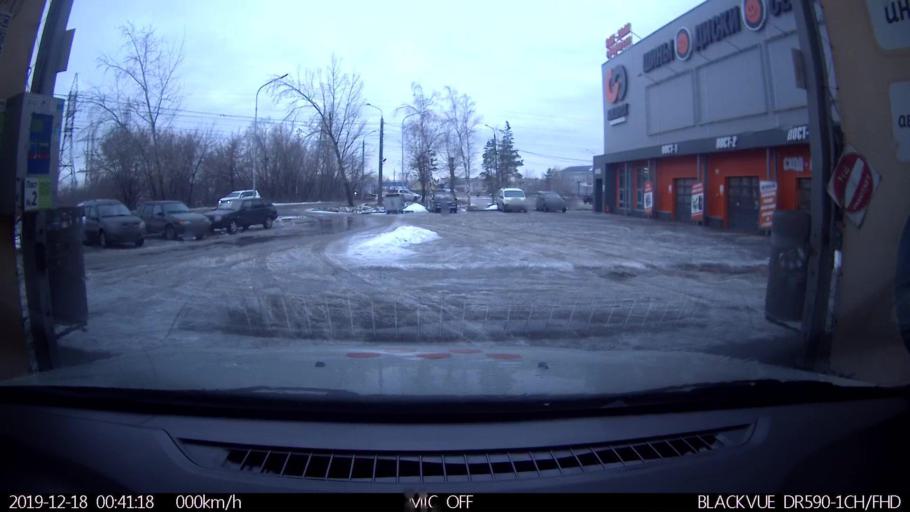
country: RU
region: Nizjnij Novgorod
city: Neklyudovo
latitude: 56.3459
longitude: 43.8902
